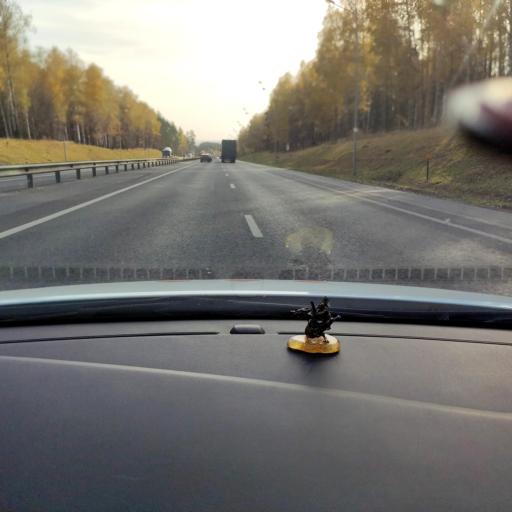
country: RU
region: Tatarstan
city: Osinovo
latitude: 55.8349
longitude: 48.8501
